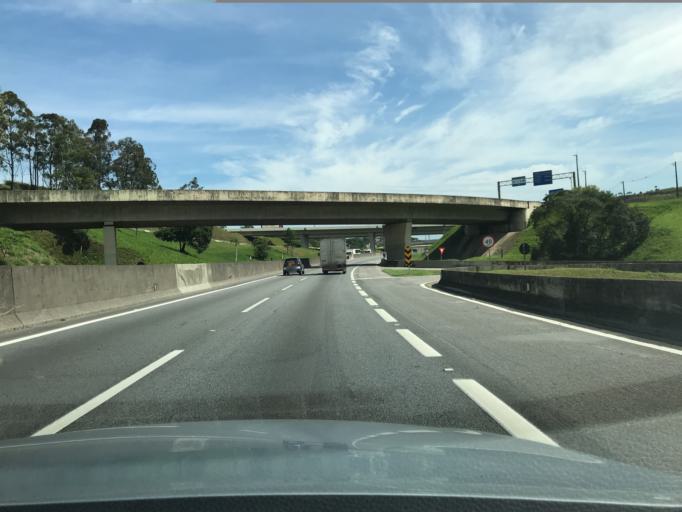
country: BR
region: Sao Paulo
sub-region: Osasco
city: Osasco
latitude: -23.4548
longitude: -46.7859
